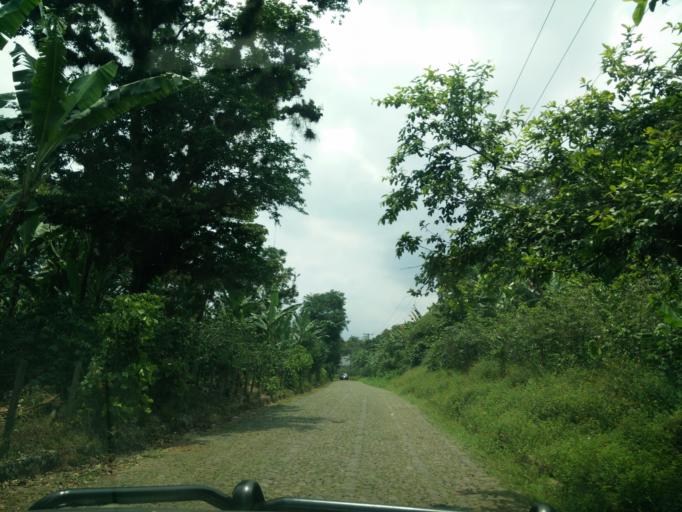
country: MX
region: Veracruz
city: Xico
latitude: 19.4095
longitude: -96.9904
